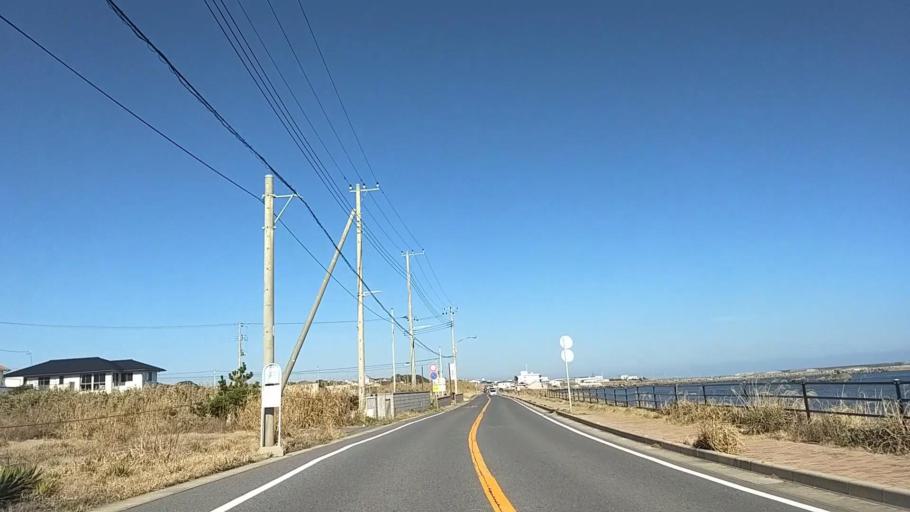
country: JP
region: Chiba
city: Hasaki
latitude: 35.7225
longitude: 140.8687
